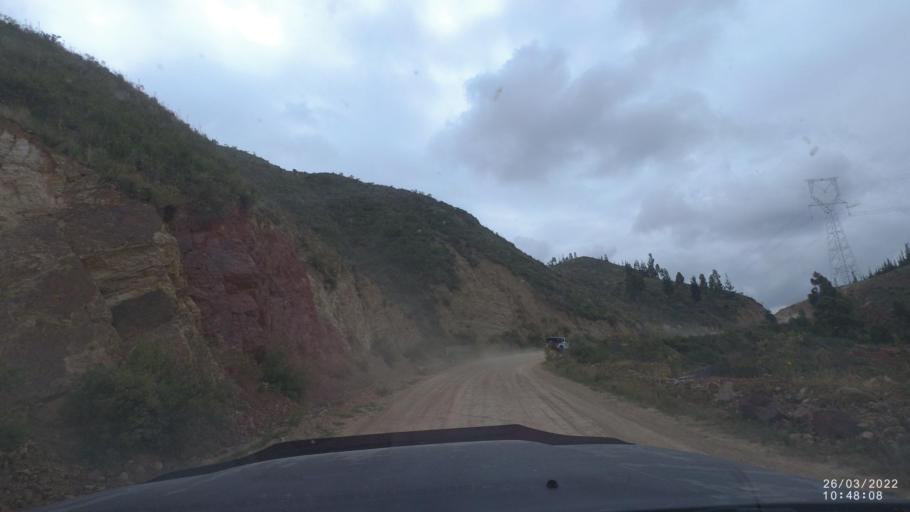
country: BO
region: Cochabamba
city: Tarata
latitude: -17.4946
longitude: -66.0461
